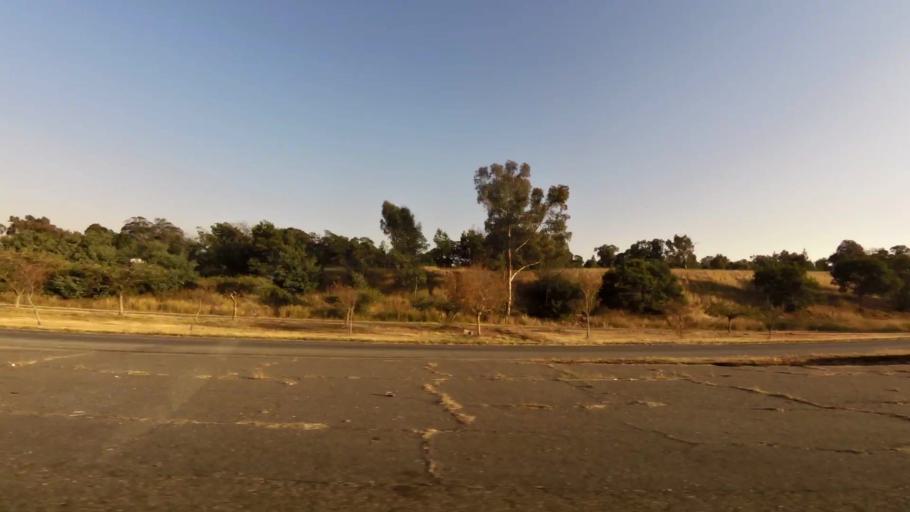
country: ZA
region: Gauteng
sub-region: City of Johannesburg Metropolitan Municipality
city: Johannesburg
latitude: -26.2611
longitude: 27.9822
